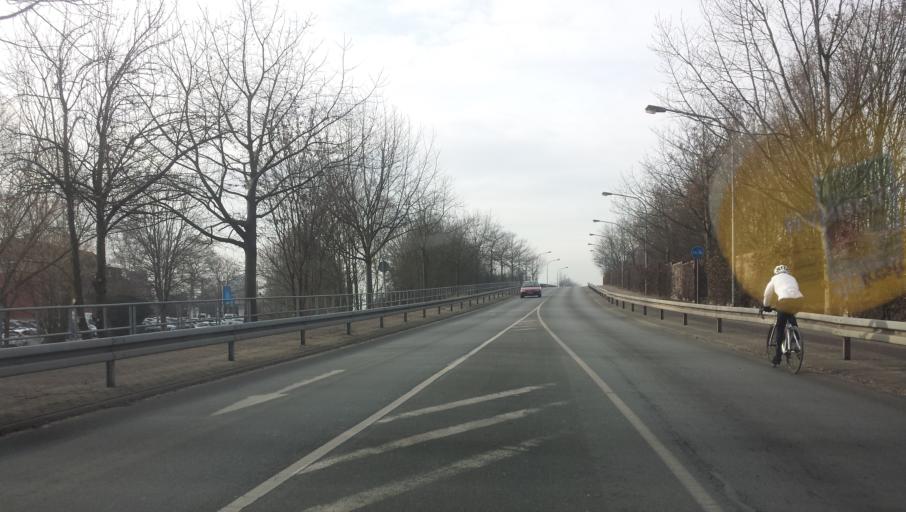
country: DE
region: Hesse
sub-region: Regierungsbezirk Darmstadt
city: Heppenheim an der Bergstrasse
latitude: 49.6493
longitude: 8.6333
